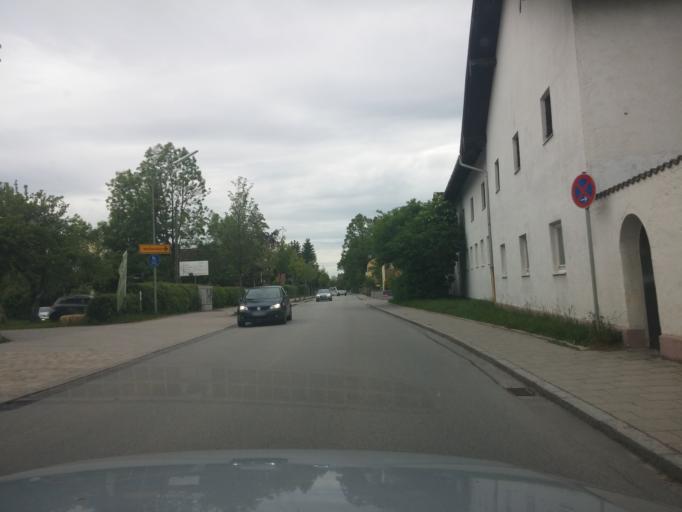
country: DE
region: Bavaria
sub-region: Upper Bavaria
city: Feldkirchen
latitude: 48.1284
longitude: 11.7404
